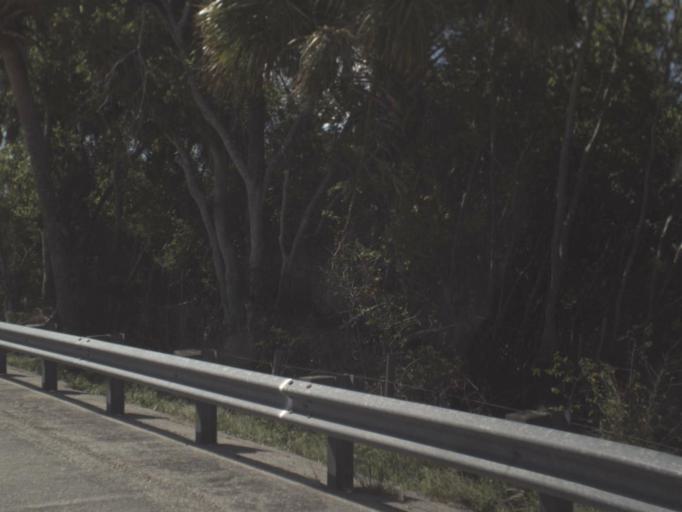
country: US
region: Florida
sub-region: Glades County
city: Buckhead Ridge
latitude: 27.0916
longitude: -80.9601
